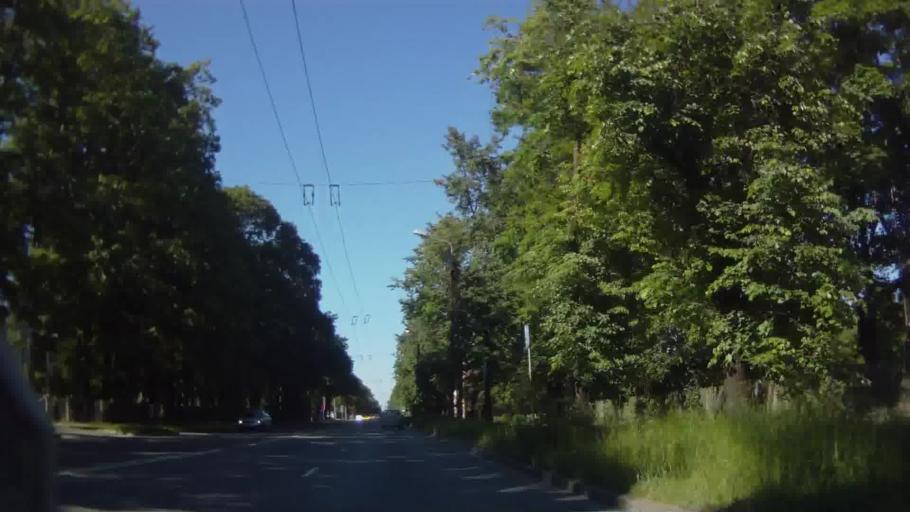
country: LV
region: Riga
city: Riga
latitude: 56.9142
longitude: 24.0872
